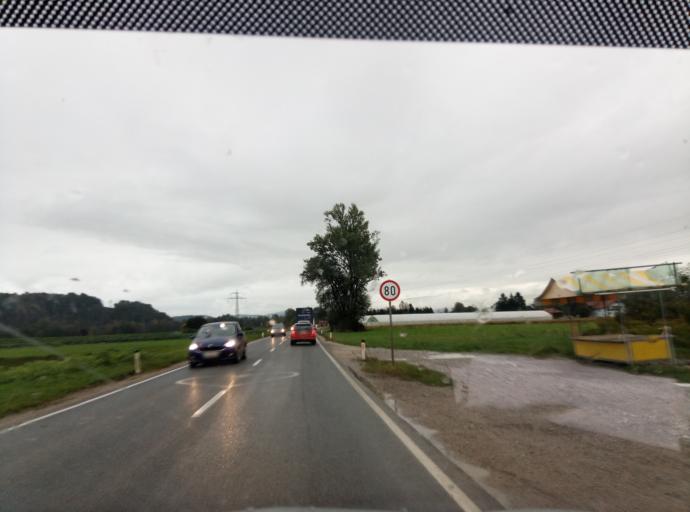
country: SI
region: Ljubljana
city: Ljubljana
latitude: 46.1025
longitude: 14.5034
